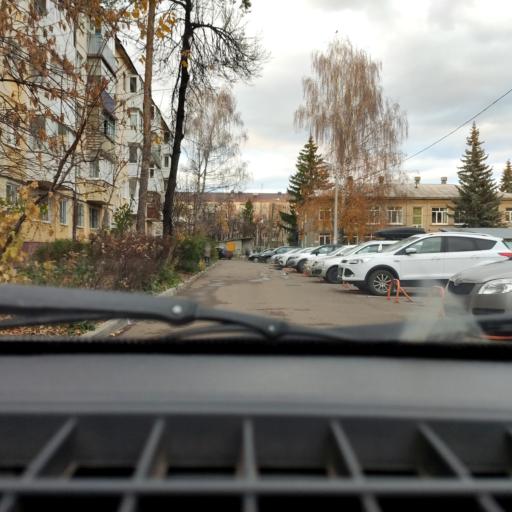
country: RU
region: Bashkortostan
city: Ufa
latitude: 54.7551
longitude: 55.9955
